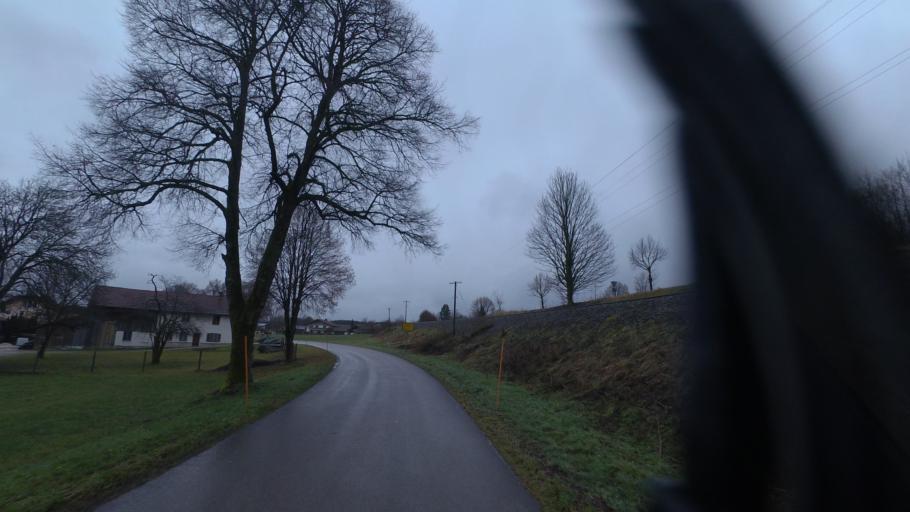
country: DE
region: Bavaria
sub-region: Upper Bavaria
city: Nussdorf
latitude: 47.9088
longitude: 12.6130
